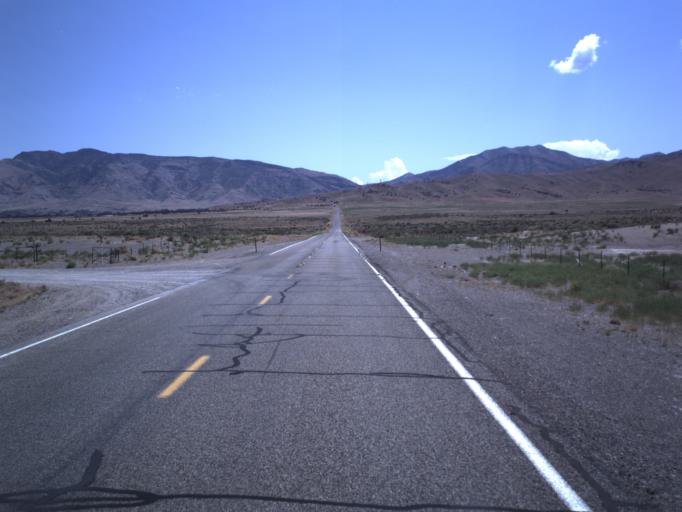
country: US
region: Utah
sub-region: Millard County
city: Delta
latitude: 39.3545
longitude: -112.4005
